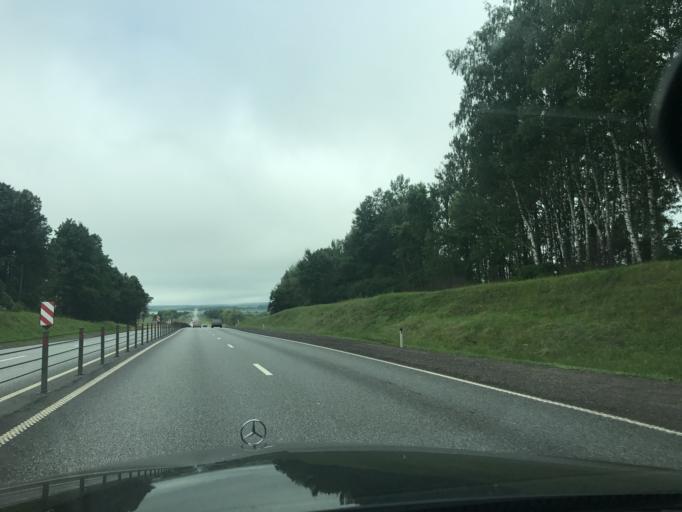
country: RU
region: Smolensk
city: Vyaz'ma
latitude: 55.3559
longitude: 34.6376
